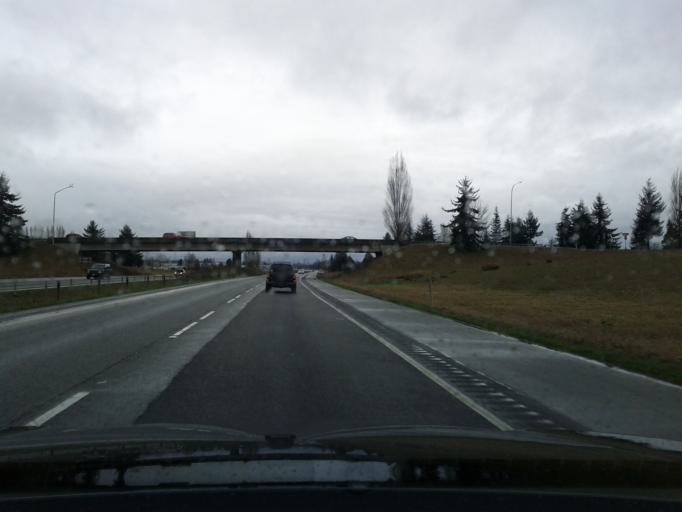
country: US
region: Washington
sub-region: Skagit County
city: Mount Vernon
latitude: 48.4008
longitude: -122.3307
